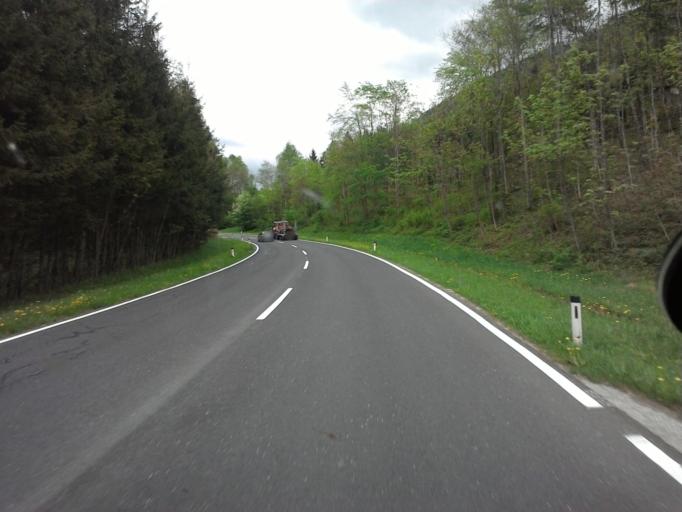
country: AT
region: Upper Austria
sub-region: Politischer Bezirk Kirchdorf an der Krems
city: Rossleithen
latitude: 47.7540
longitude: 14.2251
